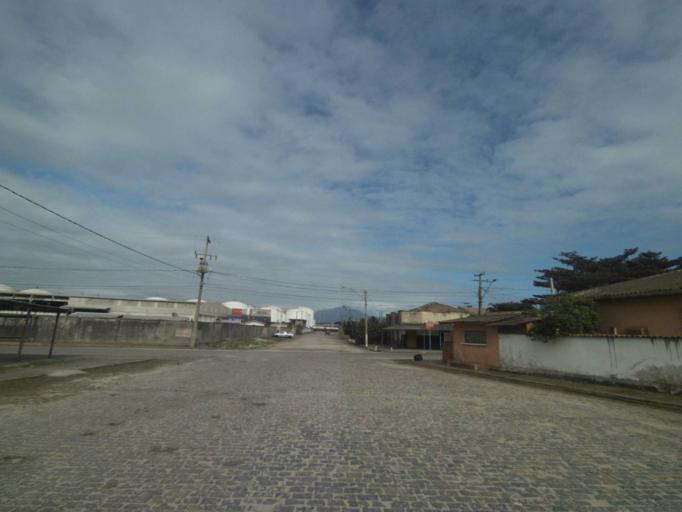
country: BR
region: Parana
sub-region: Paranagua
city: Paranagua
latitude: -25.5077
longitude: -48.5301
